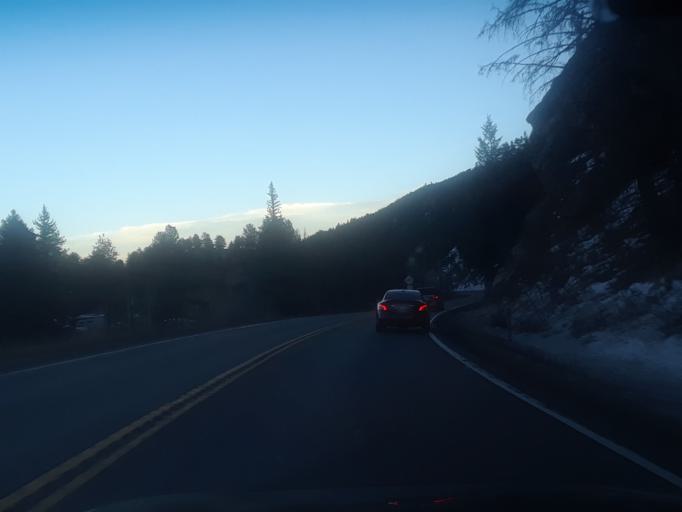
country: US
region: Colorado
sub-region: Clear Creek County
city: Georgetown
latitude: 39.4466
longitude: -105.6167
